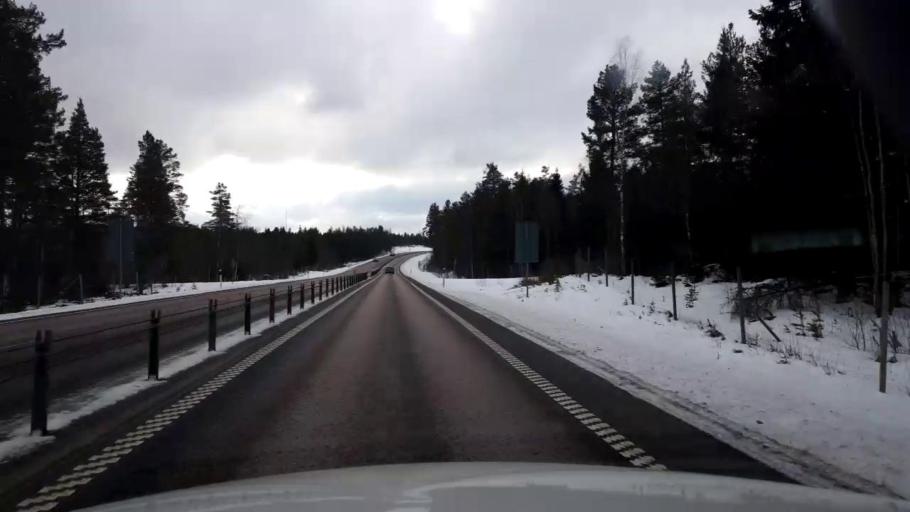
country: SE
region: Gaevleborg
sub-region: Hudiksvalls Kommun
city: Hudiksvall
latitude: 61.8156
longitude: 17.1895
